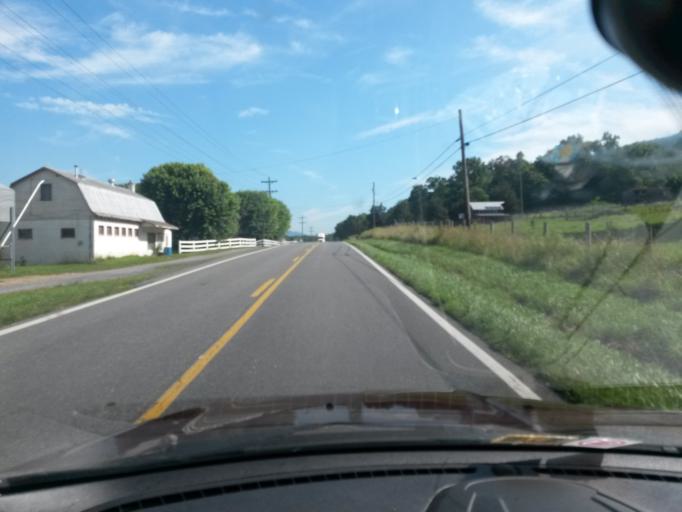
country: US
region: Virginia
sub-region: Rockingham County
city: Broadway
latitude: 38.6896
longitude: -78.9225
